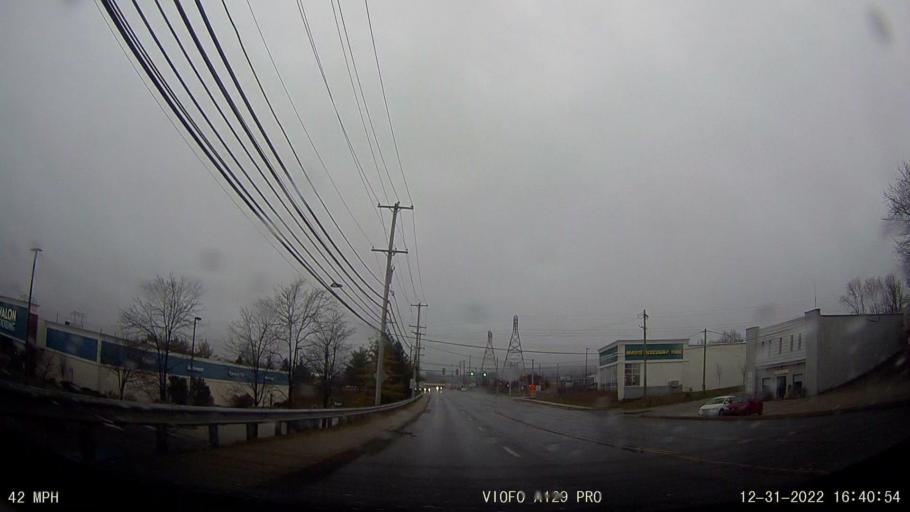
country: US
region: Pennsylvania
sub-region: Montgomery County
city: Bridgeport
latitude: 40.0912
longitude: -75.3603
